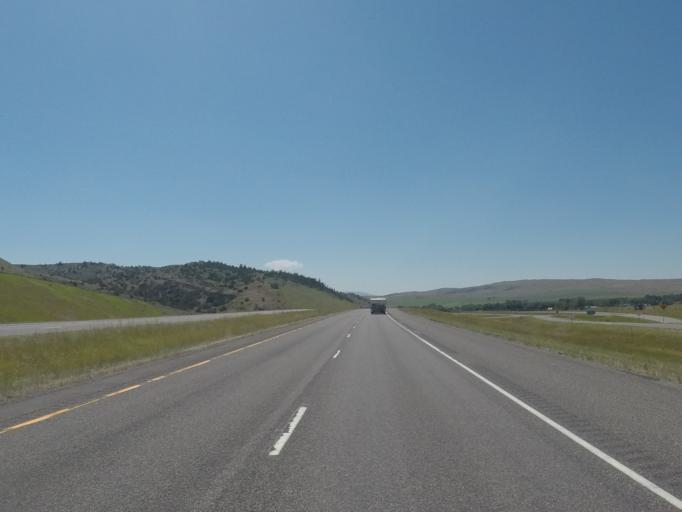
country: US
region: Montana
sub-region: Sweet Grass County
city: Big Timber
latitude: 45.7381
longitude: -110.2107
